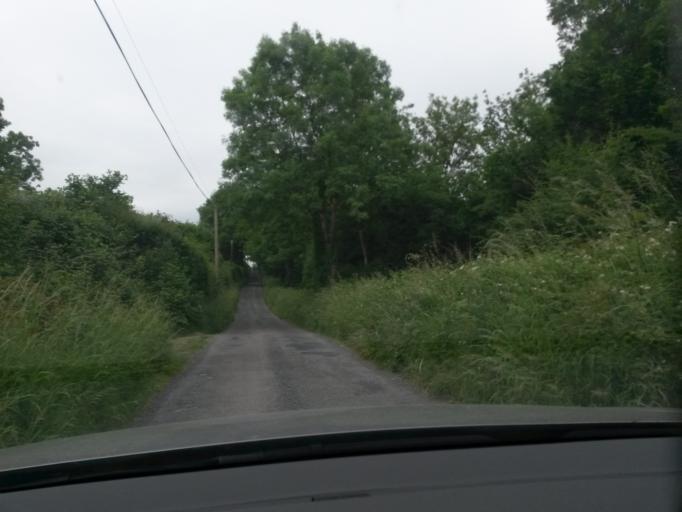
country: IE
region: Munster
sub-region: An Clar
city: Ennis
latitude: 52.9162
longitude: -9.0477
